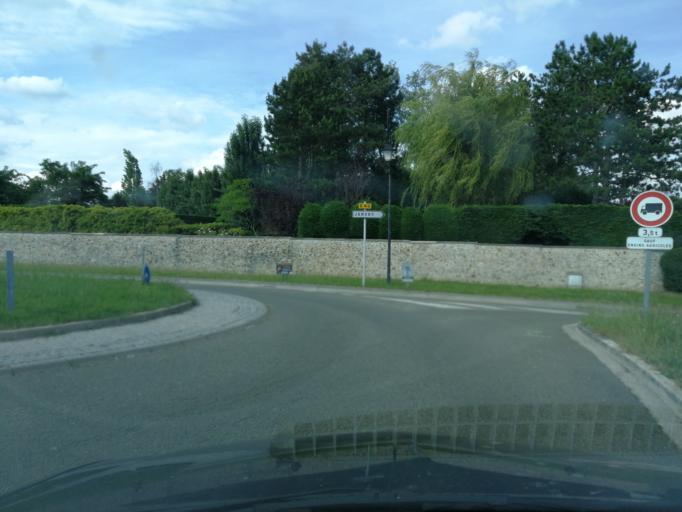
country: FR
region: Ile-de-France
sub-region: Departement de l'Essonne
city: Gometz-la-Ville
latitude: 48.6694
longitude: 2.1292
